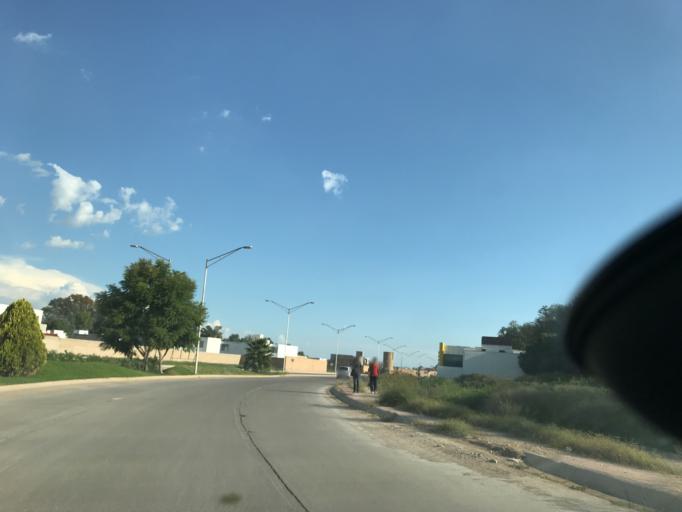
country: MX
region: Aguascalientes
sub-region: Aguascalientes
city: Pocitos
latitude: 21.9055
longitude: -102.3306
